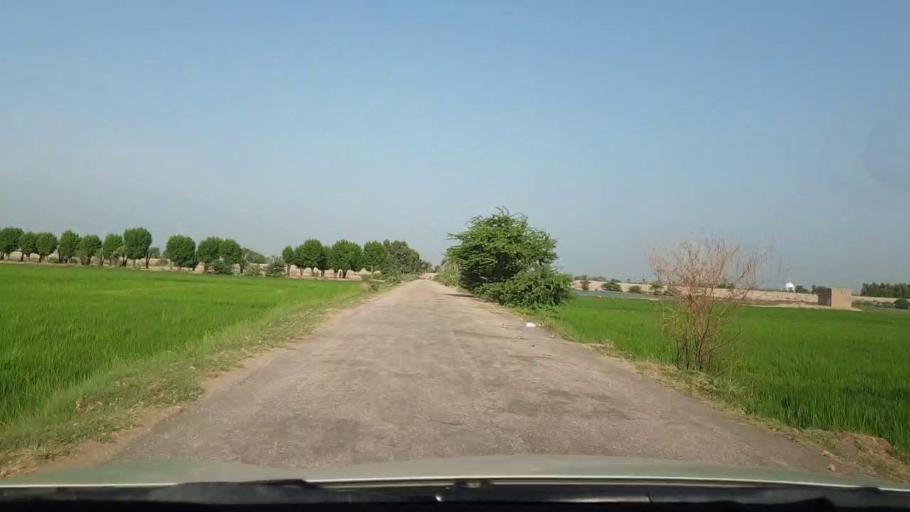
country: PK
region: Sindh
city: Larkana
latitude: 27.5455
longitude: 68.2592
